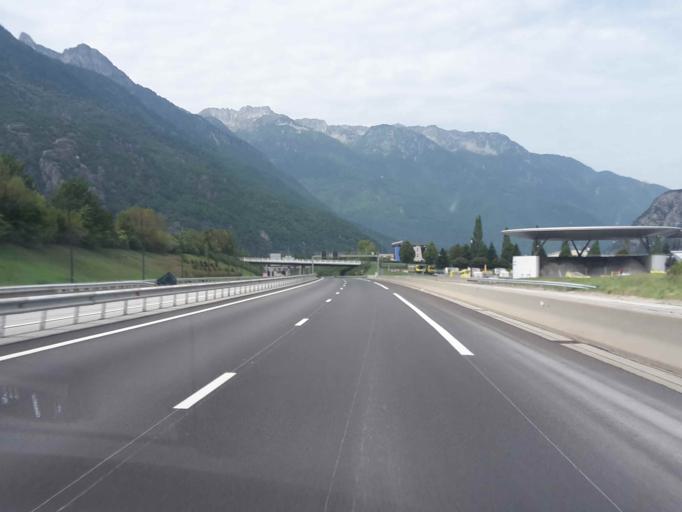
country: FR
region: Rhone-Alpes
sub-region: Departement de la Savoie
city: La Chambre
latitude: 45.3439
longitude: 6.3057
